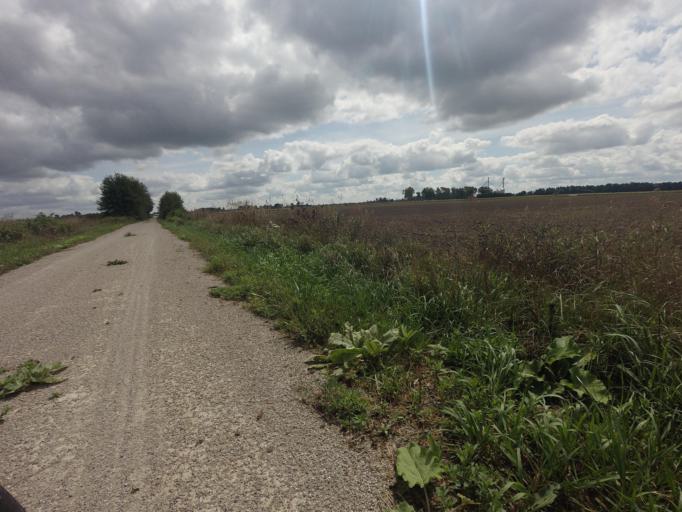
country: CA
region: Ontario
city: North Perth
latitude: 43.5655
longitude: -81.0224
